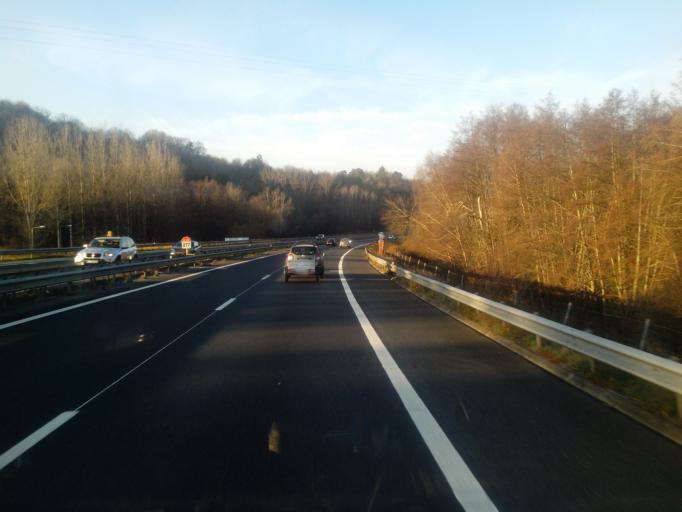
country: FR
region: Limousin
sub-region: Departement de la Correze
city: Brive-la-Gaillarde
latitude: 45.1275
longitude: 1.4931
